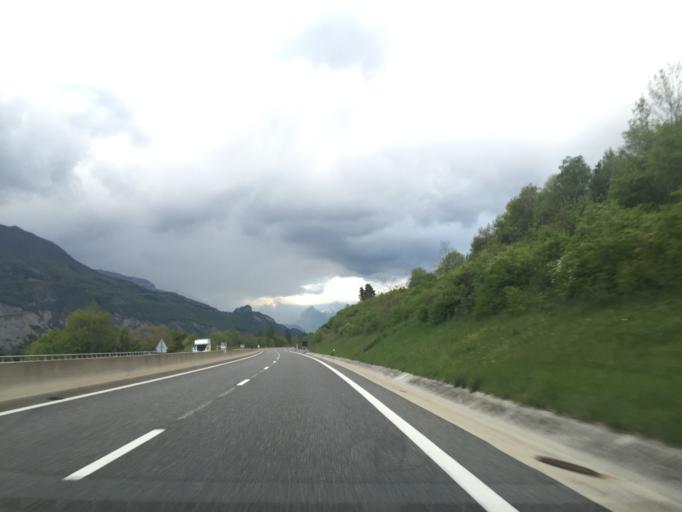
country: FR
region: Rhone-Alpes
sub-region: Departement de l'Isere
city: Le Gua
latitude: 45.0120
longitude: 5.6580
